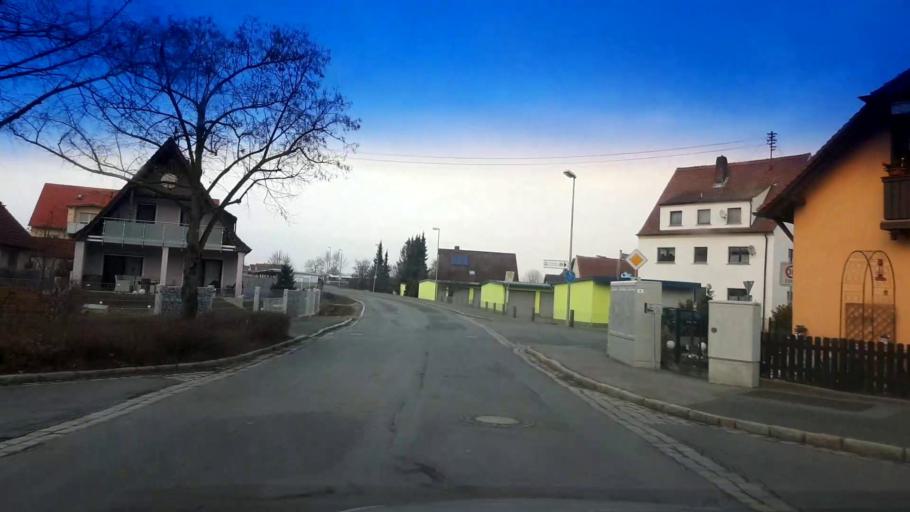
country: DE
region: Bavaria
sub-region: Upper Franconia
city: Hirschaid
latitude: 49.8089
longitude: 10.9812
